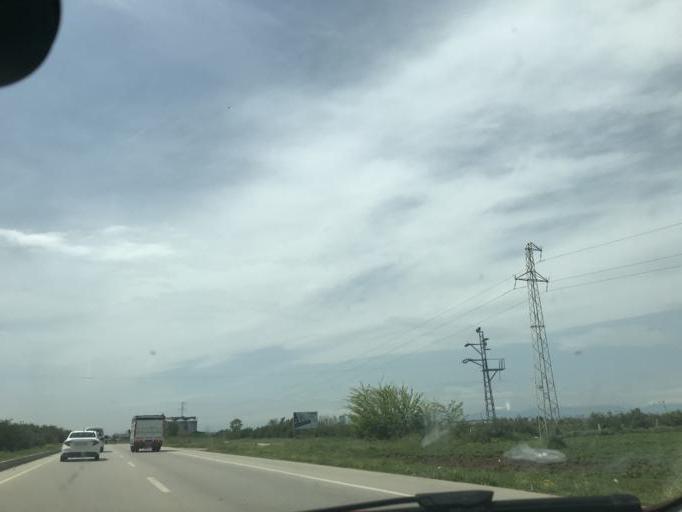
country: TR
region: Adana
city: Yuregir
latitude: 36.9768
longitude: 35.4776
